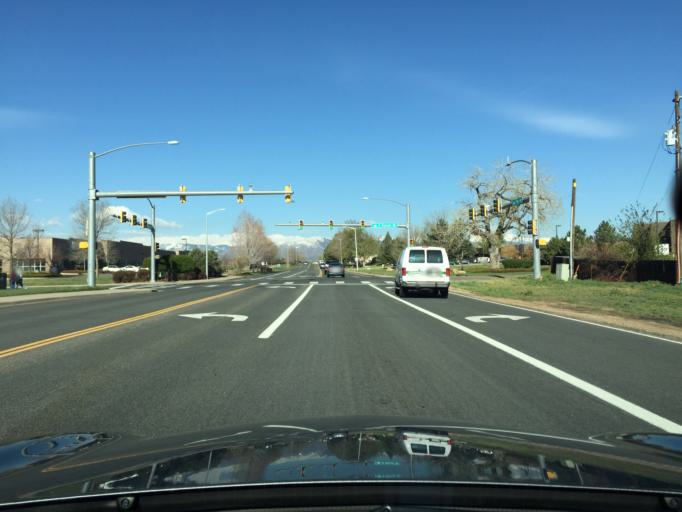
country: US
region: Colorado
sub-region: Boulder County
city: Longmont
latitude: 40.1379
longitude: -105.1208
